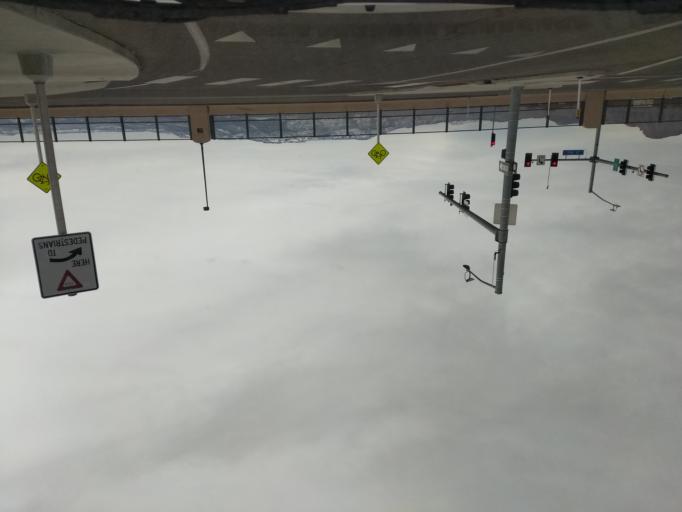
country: US
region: Colorado
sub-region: Mesa County
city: Fruitvale
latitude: 39.0725
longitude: -108.5156
